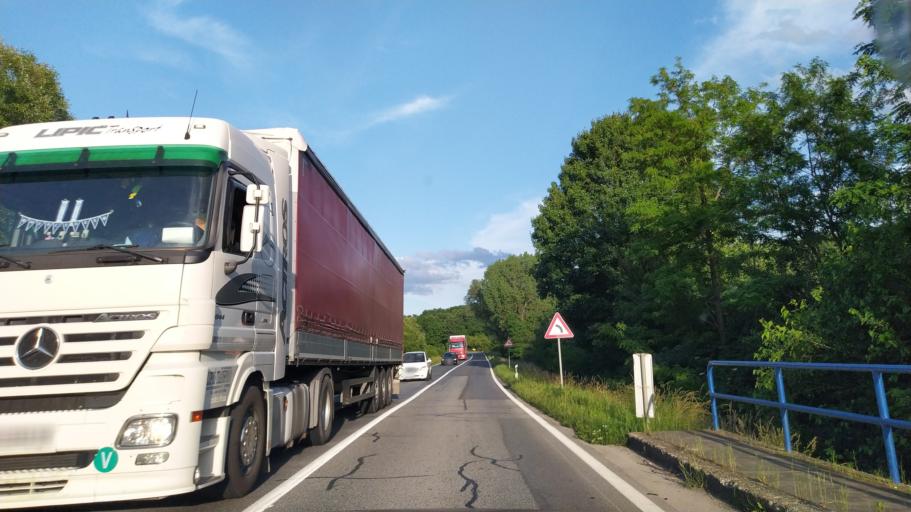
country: HR
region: Virovitick-Podravska
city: Cacinci
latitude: 45.6006
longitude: 17.8361
